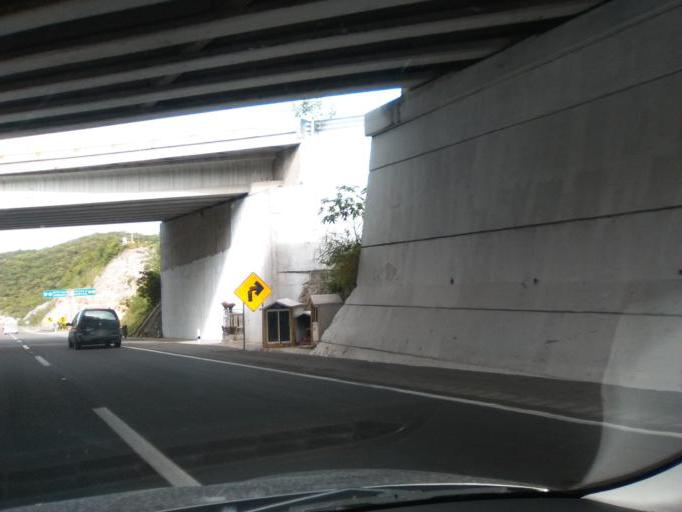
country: MX
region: Guerrero
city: Zumpango del Rio
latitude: 17.6041
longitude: -99.5185
